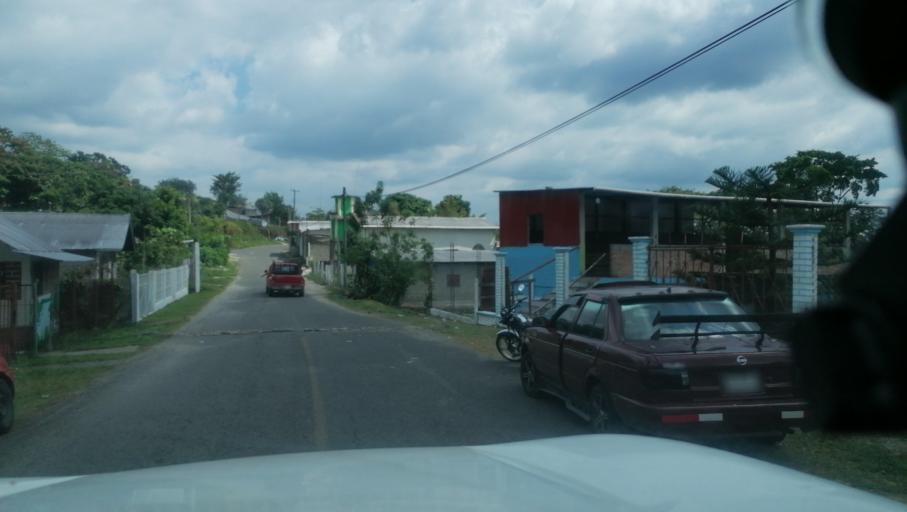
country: MX
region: Chiapas
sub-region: Cacahoatan
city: Benito Juarez
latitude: 15.0445
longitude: -92.1528
